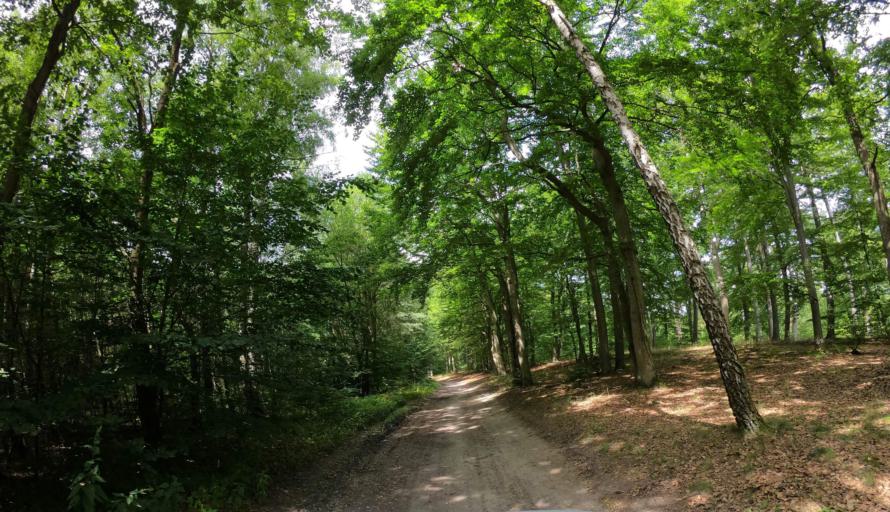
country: PL
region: West Pomeranian Voivodeship
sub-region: Powiat gryfinski
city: Stare Czarnowo
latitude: 53.3378
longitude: 14.7992
